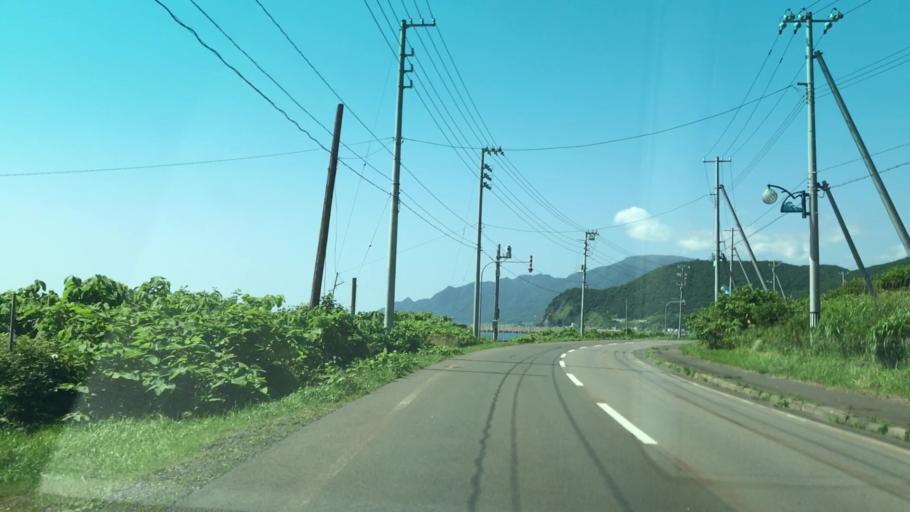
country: JP
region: Hokkaido
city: Iwanai
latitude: 43.0911
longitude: 140.4639
